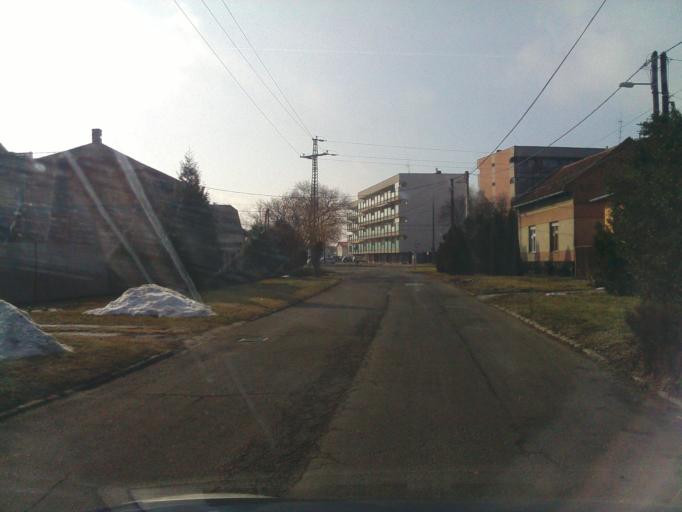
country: HU
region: Heves
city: Hatvan
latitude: 47.6688
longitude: 19.6966
